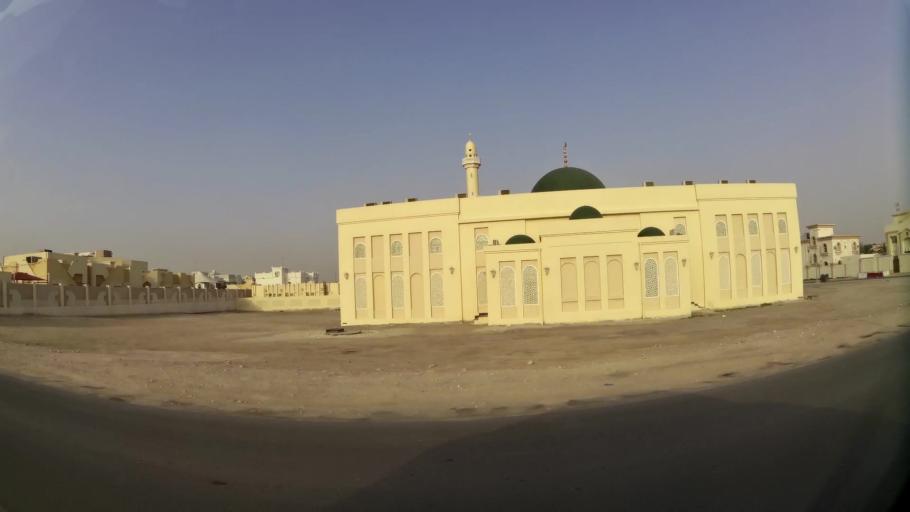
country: QA
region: Baladiyat ar Rayyan
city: Ar Rayyan
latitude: 25.2418
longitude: 51.4486
